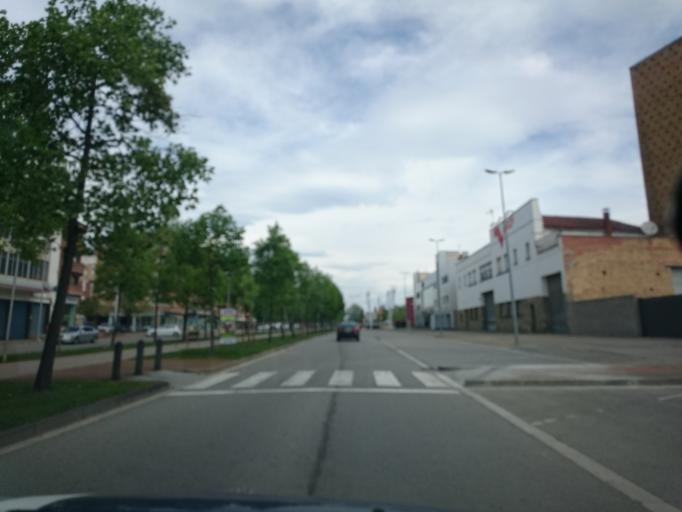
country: ES
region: Catalonia
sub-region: Provincia de Barcelona
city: Vic
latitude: 41.9287
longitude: 2.2450
